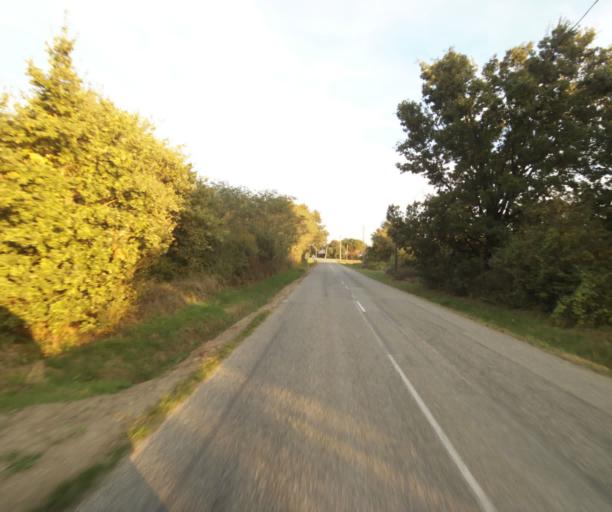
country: FR
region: Midi-Pyrenees
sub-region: Departement du Tarn-et-Garonne
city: Grisolles
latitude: 43.8331
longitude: 1.3076
